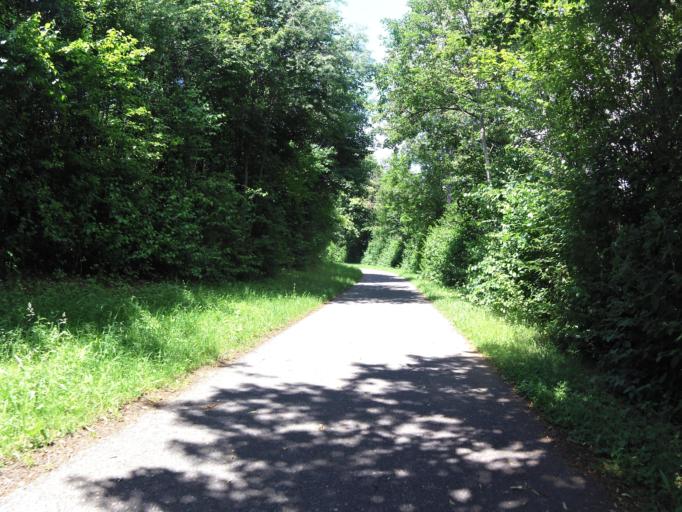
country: DE
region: Baden-Wuerttemberg
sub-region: Freiburg Region
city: Hohberg
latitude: 48.3348
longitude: 7.9124
